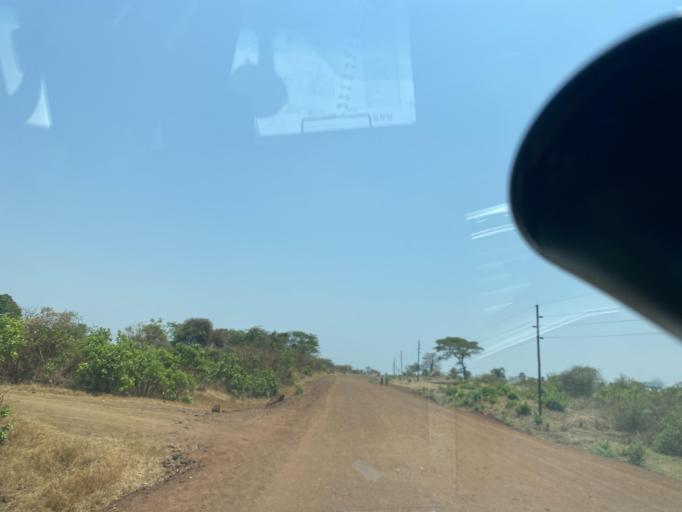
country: ZM
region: Southern
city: Nakambala
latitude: -15.4787
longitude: 27.8983
